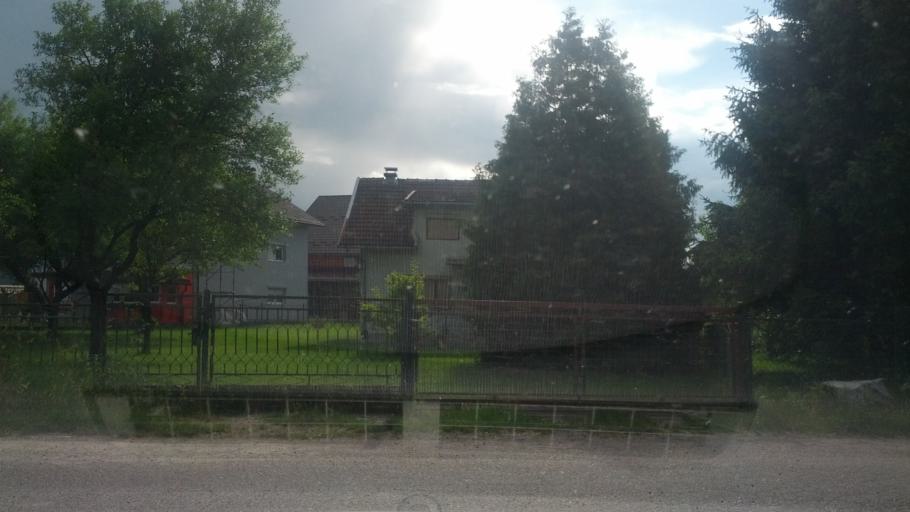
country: BA
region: Federation of Bosnia and Herzegovina
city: Bihac
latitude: 44.8412
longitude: 15.8748
